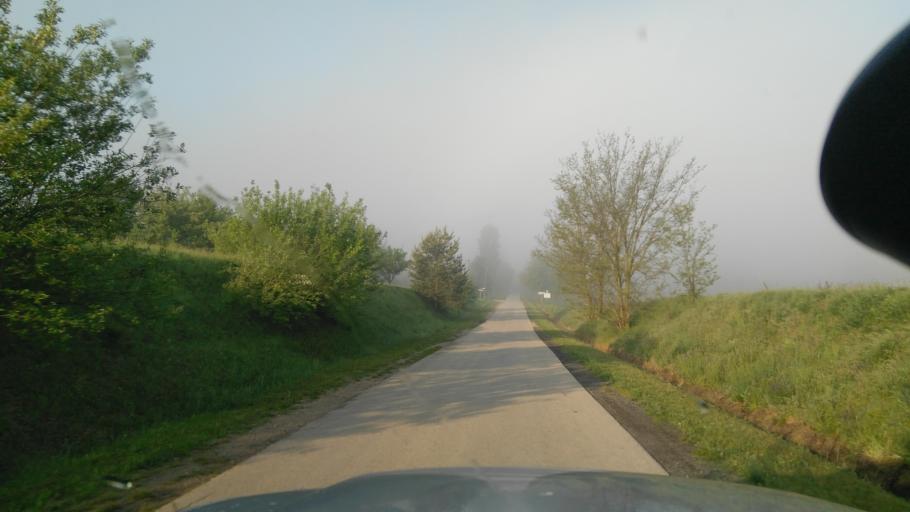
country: HU
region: Zala
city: Heviz
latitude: 46.7631
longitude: 17.1338
